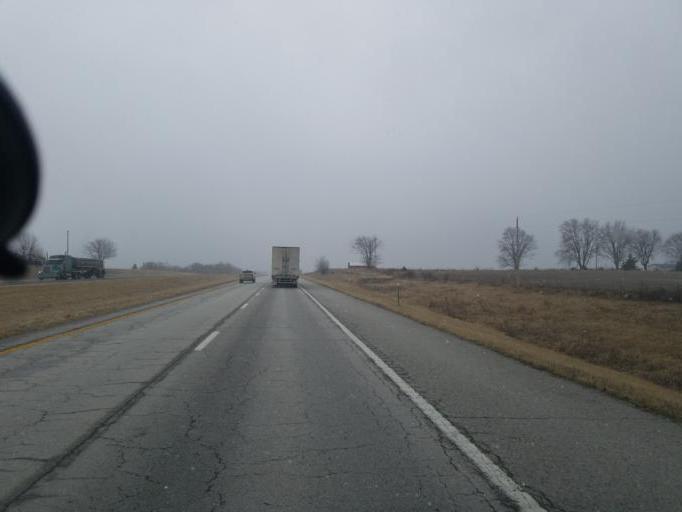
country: US
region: Missouri
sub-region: Macon County
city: La Plata
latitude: 39.9166
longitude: -92.4745
